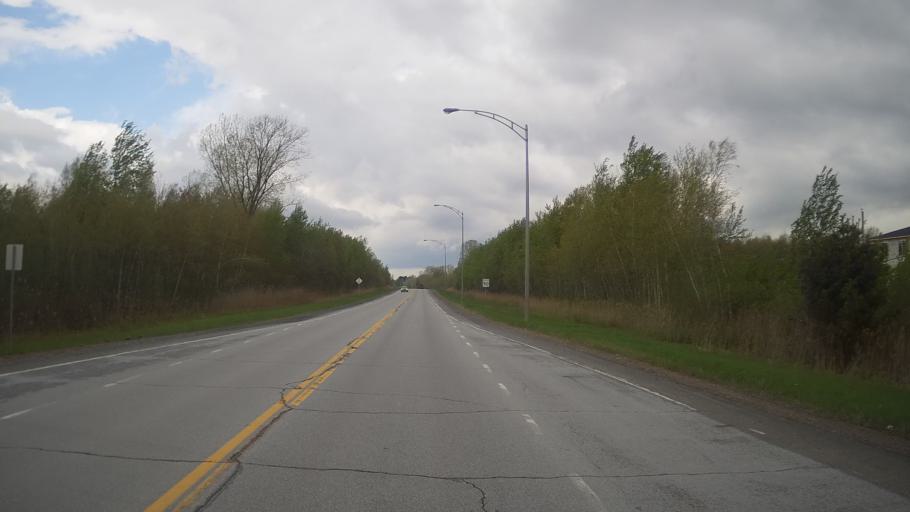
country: CA
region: Quebec
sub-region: Monteregie
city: Farnham
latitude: 45.2710
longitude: -72.9651
